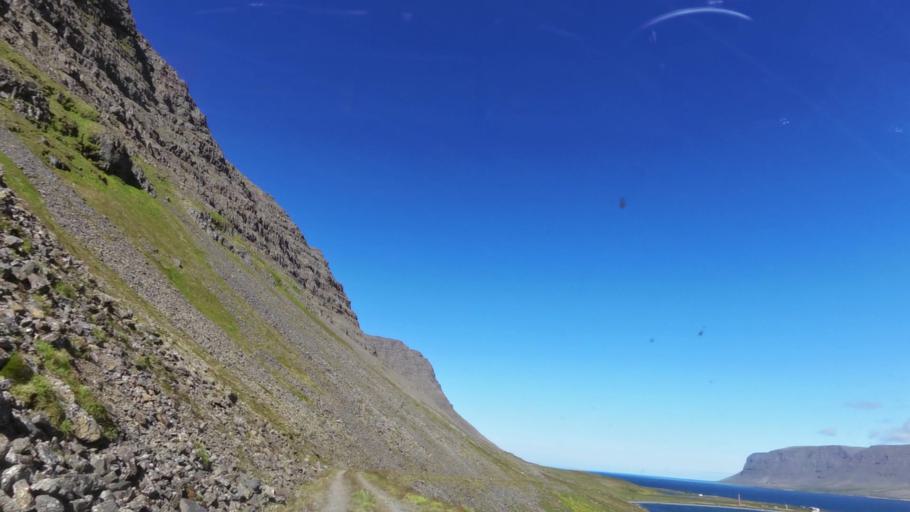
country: IS
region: West
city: Olafsvik
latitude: 65.6328
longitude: -23.9186
